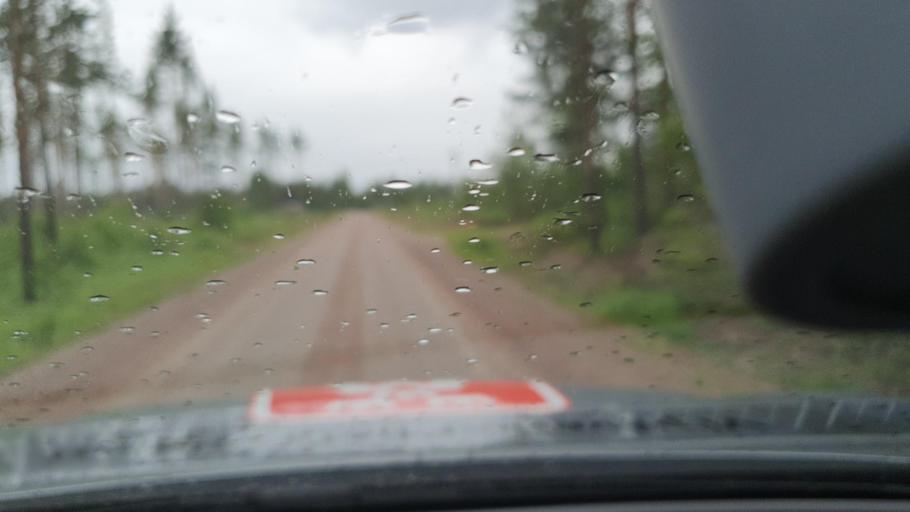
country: SE
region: Norrbotten
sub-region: Overkalix Kommun
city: OEverkalix
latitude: 66.4932
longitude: 22.7635
